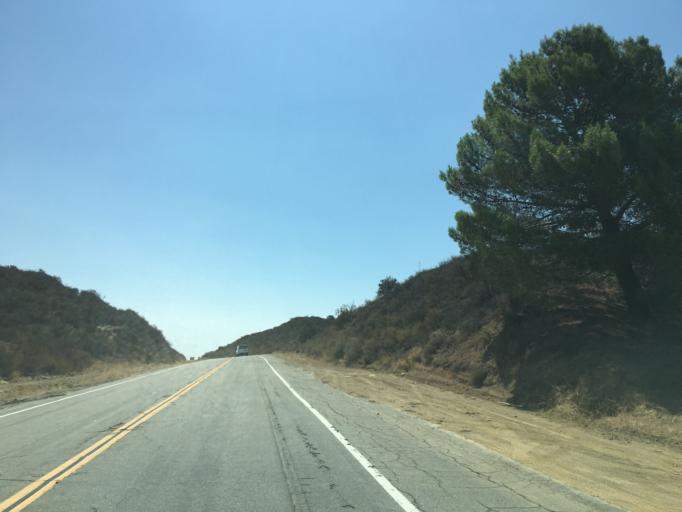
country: US
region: California
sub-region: Los Angeles County
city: Castaic
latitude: 34.5168
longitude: -118.5857
